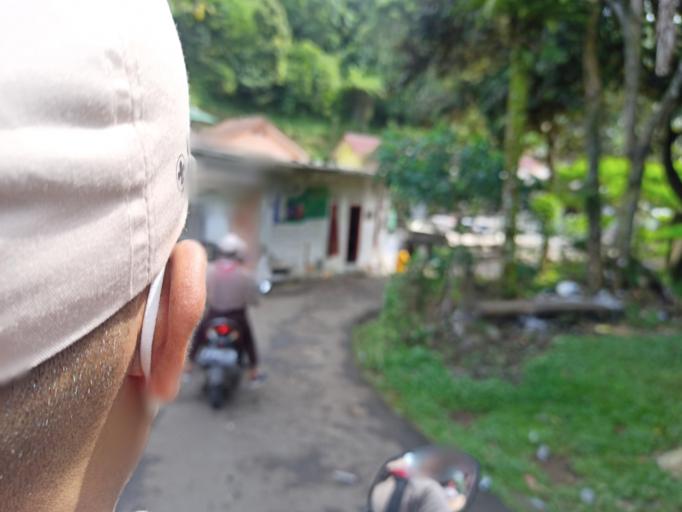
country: ID
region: West Java
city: Caringin
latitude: -6.6420
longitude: 106.9102
